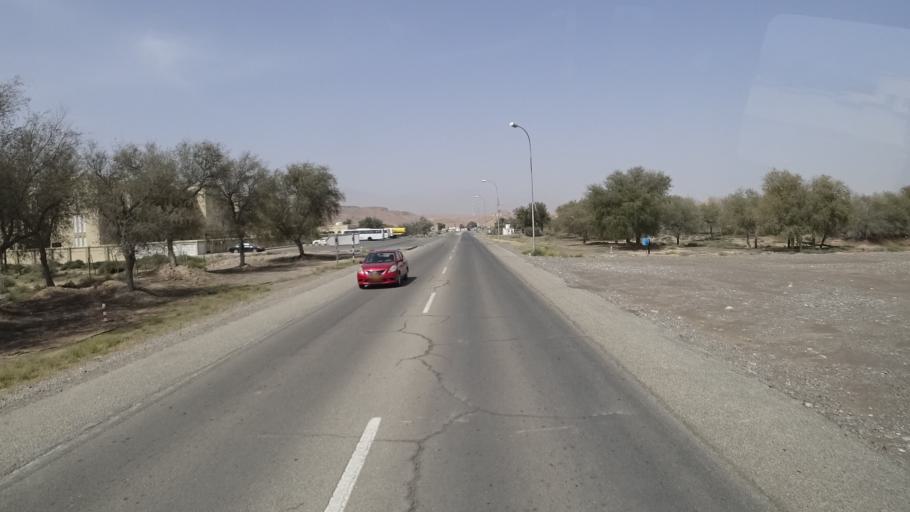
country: OM
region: Muhafazat Masqat
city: Muscat
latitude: 23.2059
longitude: 58.9587
